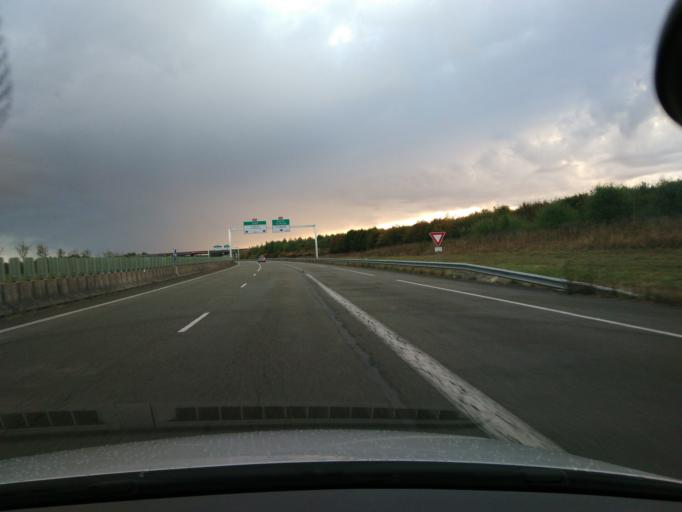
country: FR
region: Haute-Normandie
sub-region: Departement de l'Eure
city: Evreux
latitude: 49.0104
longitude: 1.1898
